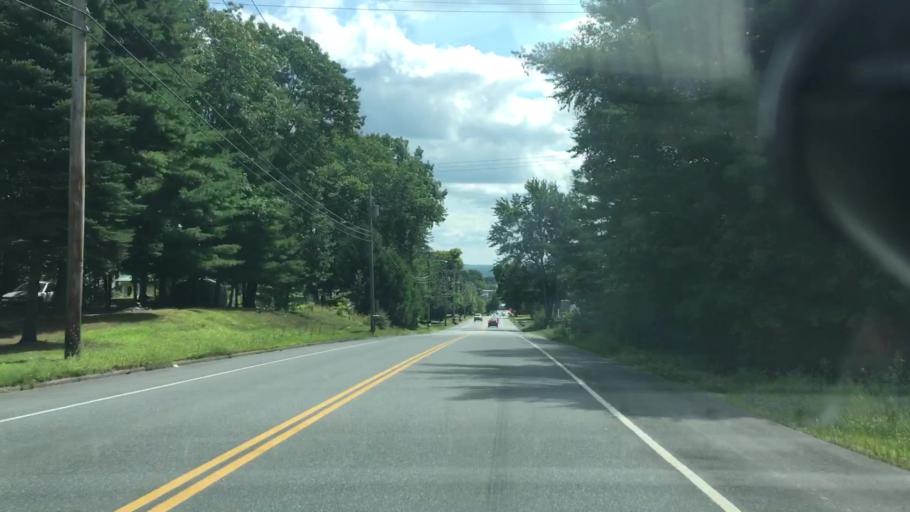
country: US
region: Maine
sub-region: Kennebec County
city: Waterville
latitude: 44.5765
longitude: -69.6440
